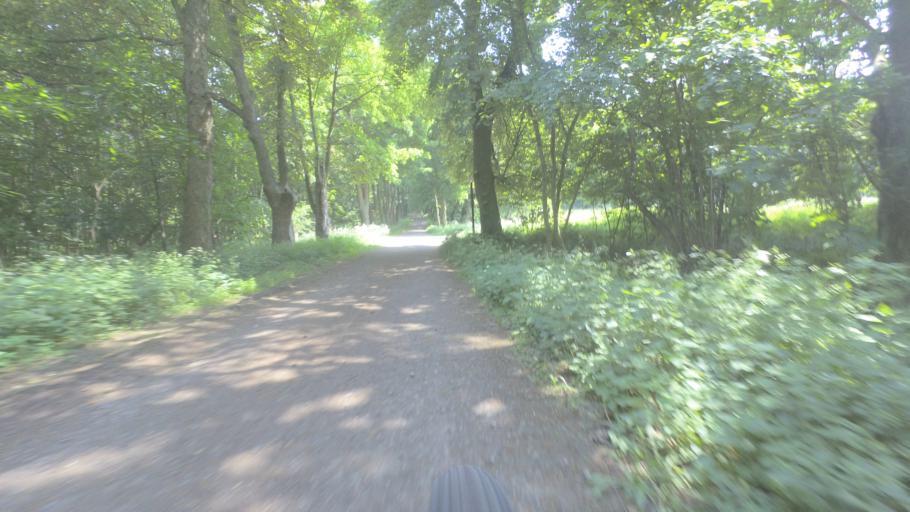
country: DE
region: Saxony-Anhalt
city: Ballenstedt
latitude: 51.7238
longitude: 11.2002
